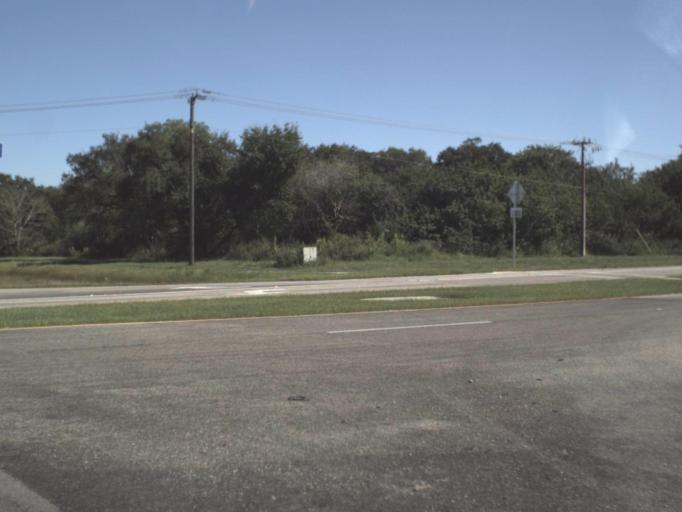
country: US
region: Florida
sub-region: Hendry County
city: Port LaBelle
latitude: 26.7620
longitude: -81.4097
